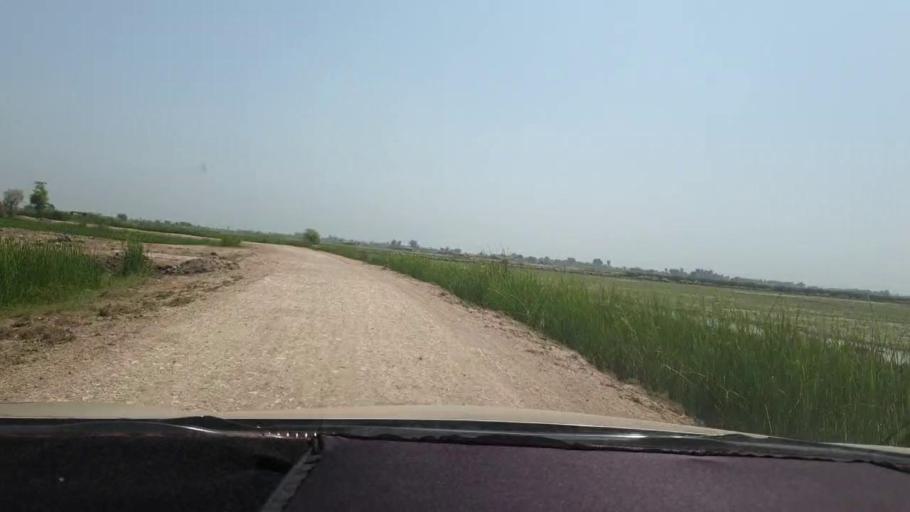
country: PK
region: Sindh
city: Shahdadkot
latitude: 27.8253
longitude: 67.9917
